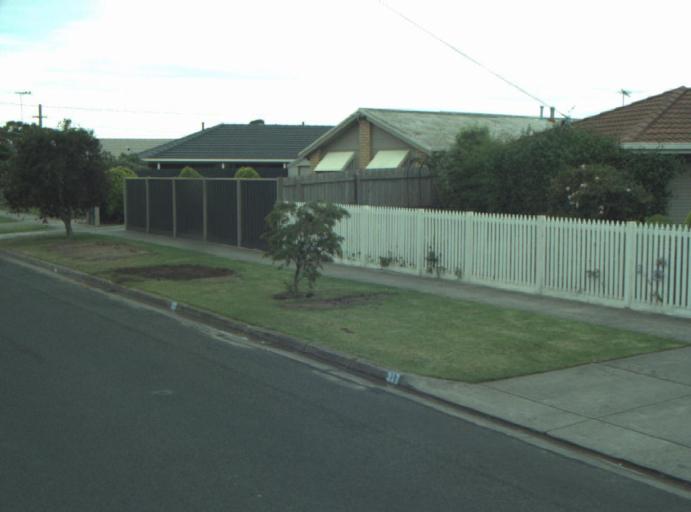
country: AU
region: Victoria
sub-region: Greater Geelong
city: Breakwater
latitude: -38.1870
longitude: 144.3884
